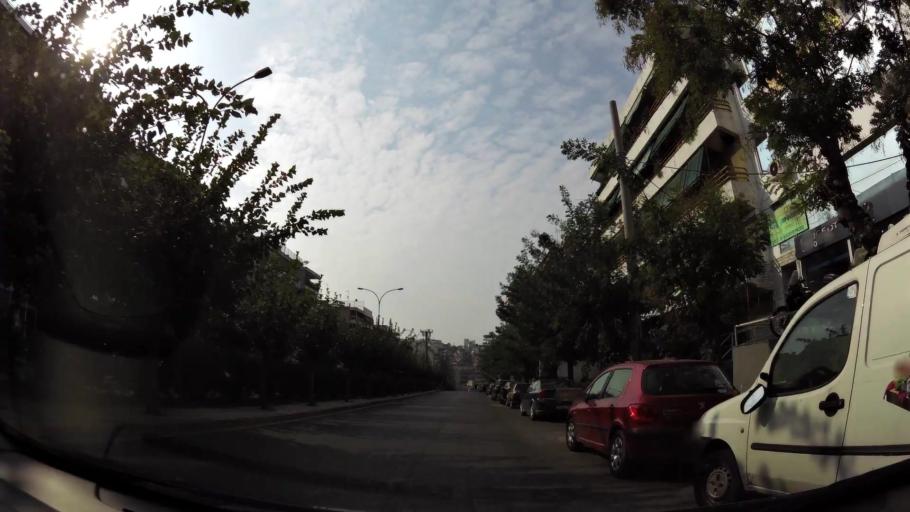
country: GR
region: Attica
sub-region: Nomarchia Athinas
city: Kipseli
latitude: 37.9978
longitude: 23.7505
